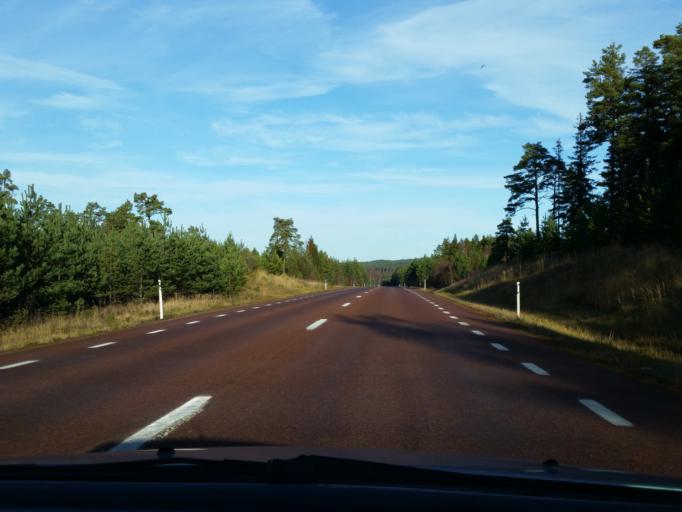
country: AX
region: Alands landsbygd
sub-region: Finstroem
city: Finstroem
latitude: 60.2870
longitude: 19.9528
